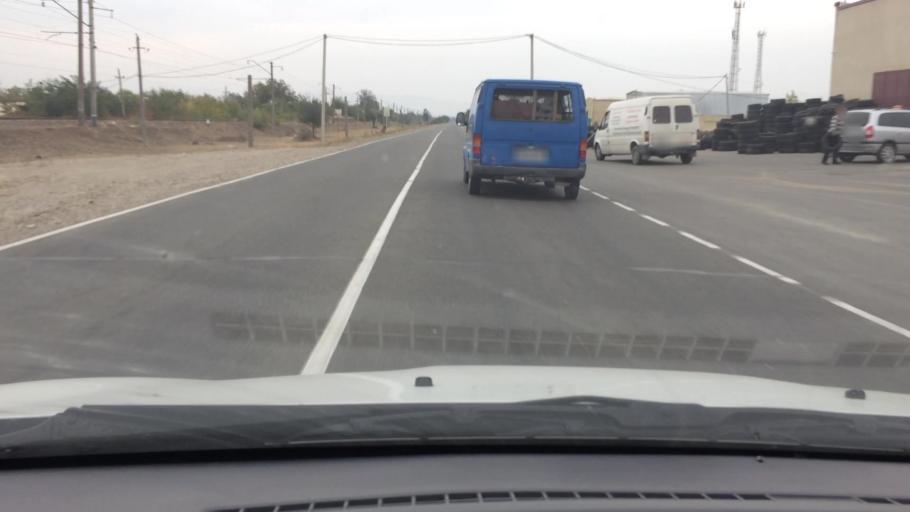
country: GE
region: Kvemo Kartli
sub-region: Marneuli
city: Marneuli
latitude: 41.4372
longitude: 44.8188
